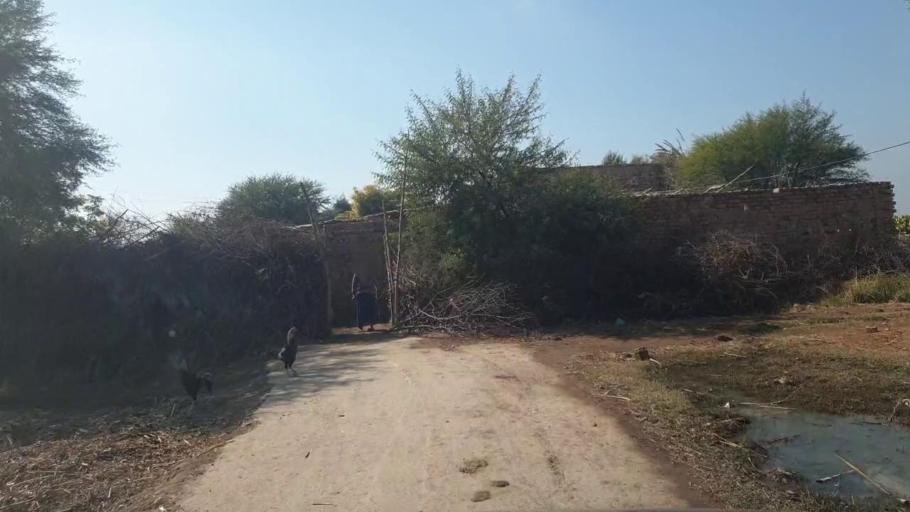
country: PK
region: Sindh
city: Shahdadpur
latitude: 25.9316
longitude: 68.5806
